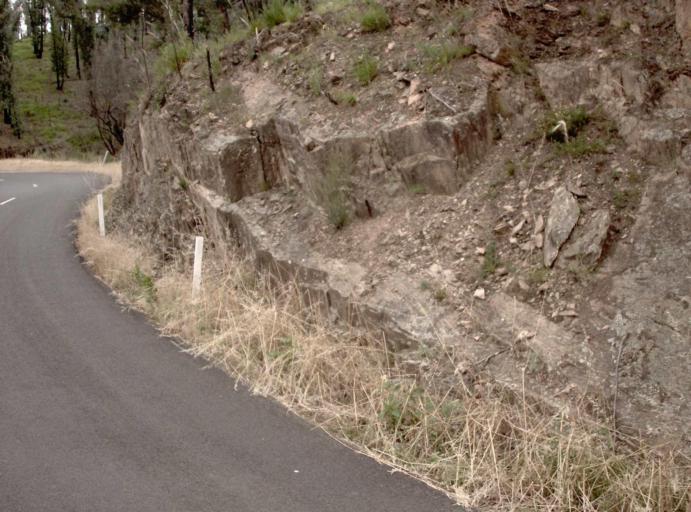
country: AU
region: Victoria
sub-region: Wellington
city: Heyfield
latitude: -37.8501
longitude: 146.7074
